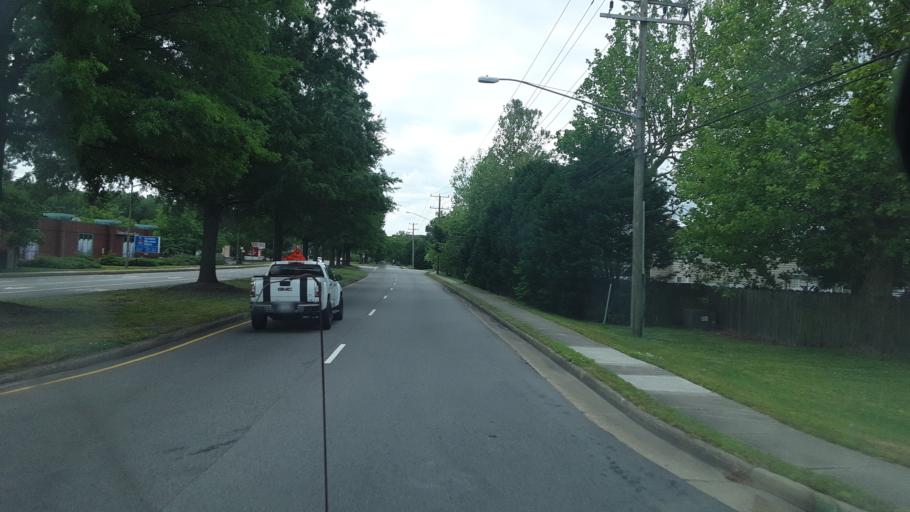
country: US
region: Virginia
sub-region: City of Virginia Beach
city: Virginia Beach
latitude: 36.7825
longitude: -76.0015
